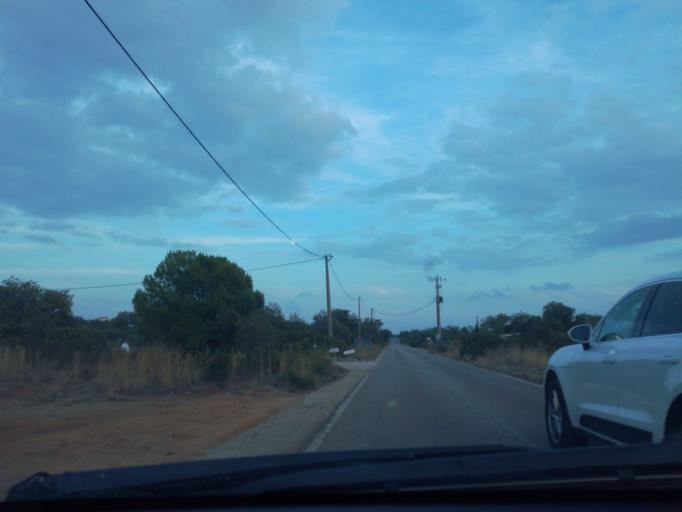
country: PT
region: Faro
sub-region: Olhao
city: Laranjeiro
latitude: 37.0799
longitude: -7.8321
